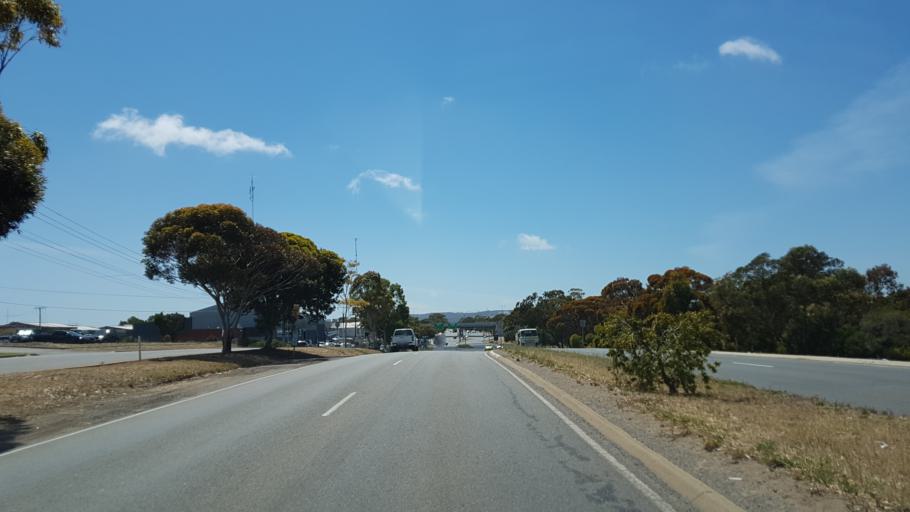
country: AU
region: South Australia
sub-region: Onkaparinga
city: Reynella
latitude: -35.1061
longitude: 138.5049
